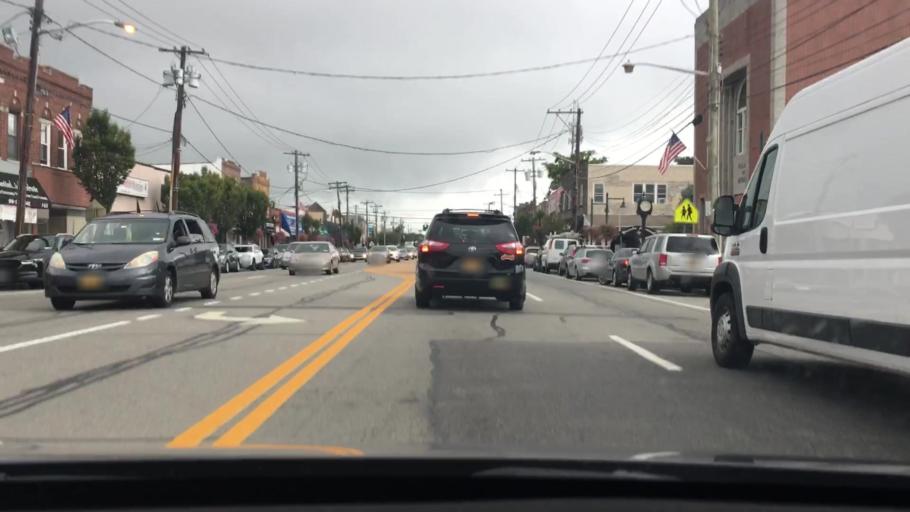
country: US
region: New York
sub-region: Nassau County
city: Mineola
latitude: 40.7486
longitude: -73.6427
